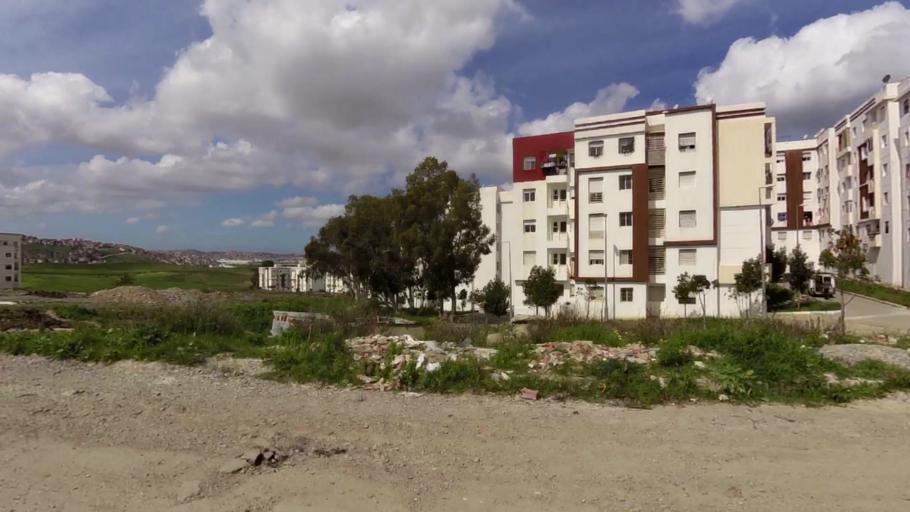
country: MA
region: Tanger-Tetouan
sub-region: Tanger-Assilah
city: Tangier
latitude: 35.7606
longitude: -5.7612
